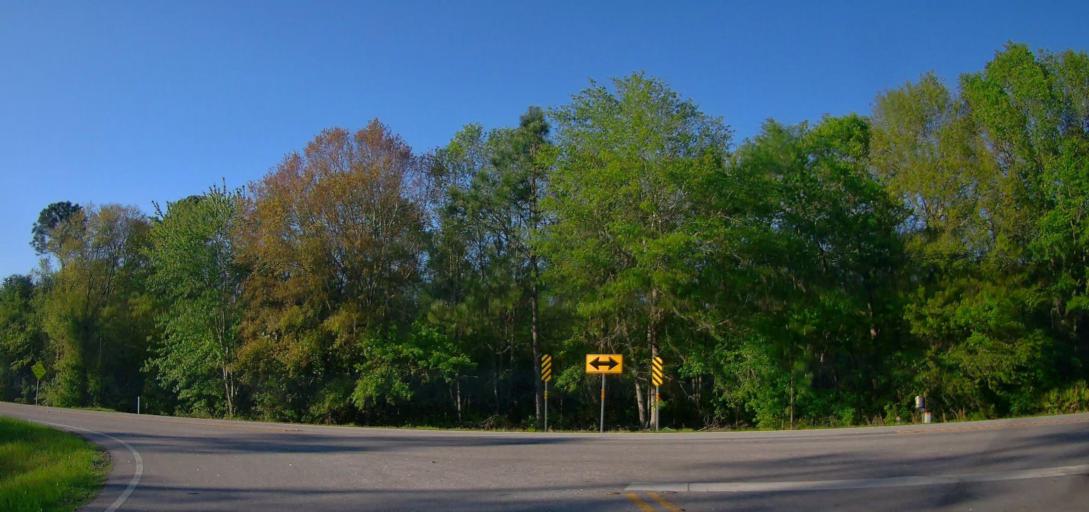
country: US
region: Georgia
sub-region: Ben Hill County
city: Fitzgerald
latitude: 31.7033
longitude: -83.1530
